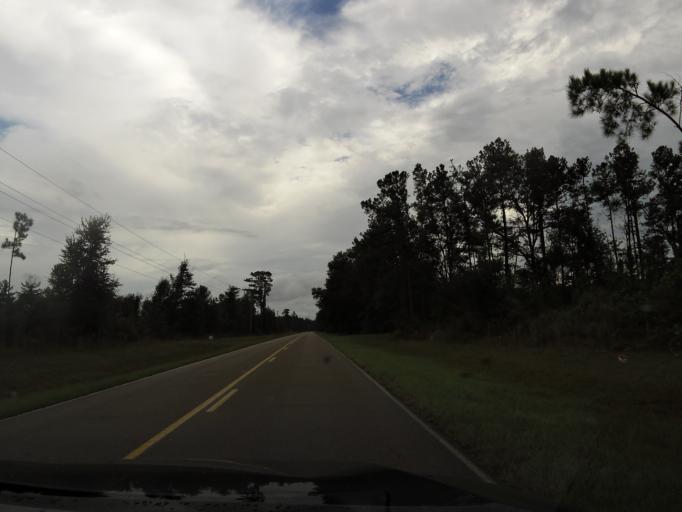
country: US
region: Florida
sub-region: Duval County
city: Baldwin
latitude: 30.4788
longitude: -81.9980
